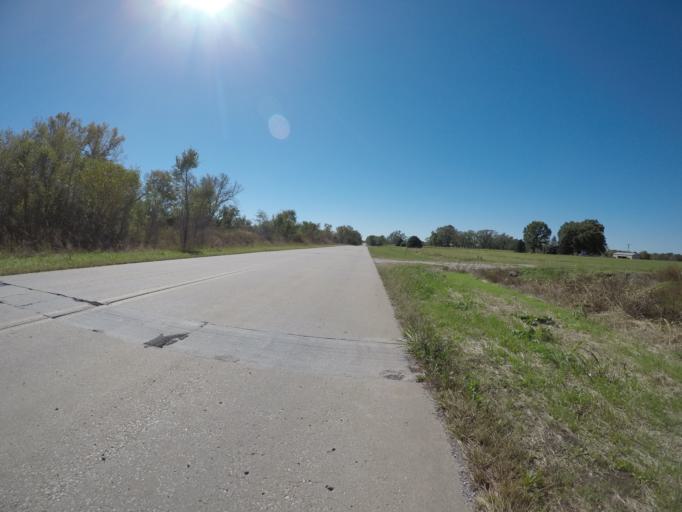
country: US
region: Kansas
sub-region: Wyandotte County
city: Bonner Springs
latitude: 39.0290
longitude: -94.8978
